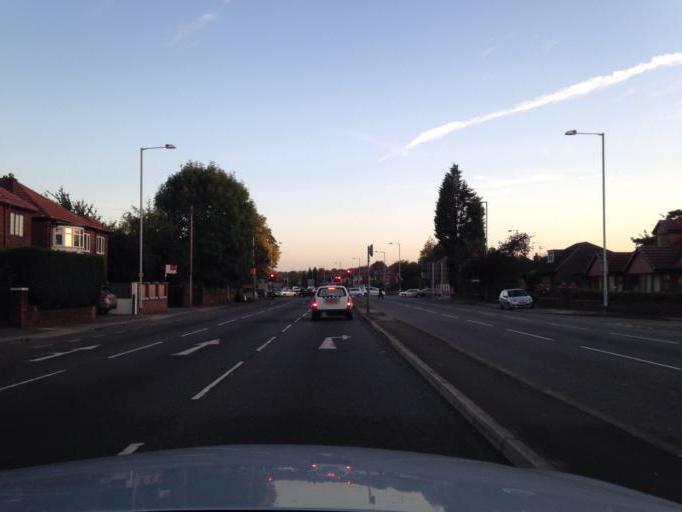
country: GB
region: England
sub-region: Manchester
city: Didsbury
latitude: 53.3928
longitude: -2.2266
